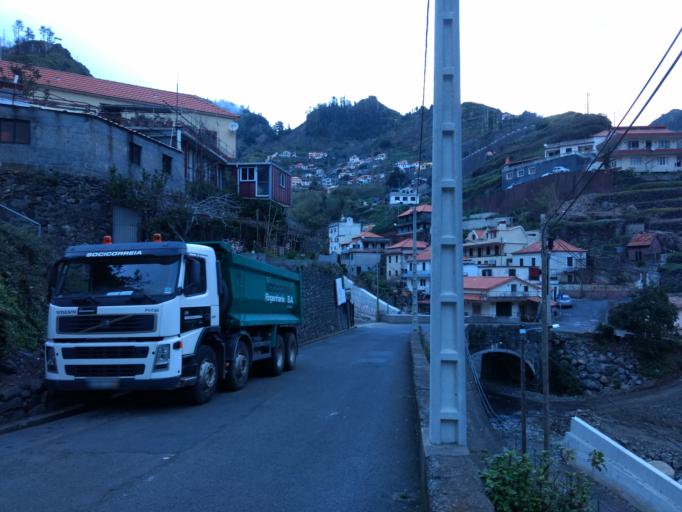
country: PT
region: Madeira
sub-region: Camara de Lobos
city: Curral das Freiras
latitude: 32.7268
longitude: -17.0280
